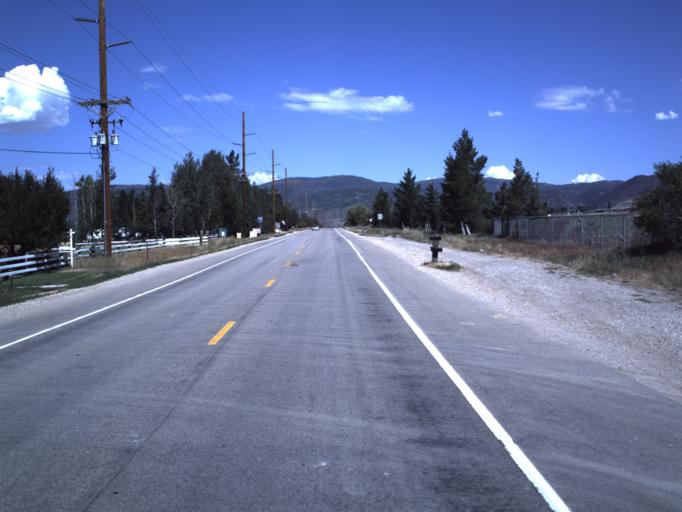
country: US
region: Utah
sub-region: Summit County
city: Kamas
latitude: 40.6773
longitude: -111.2809
